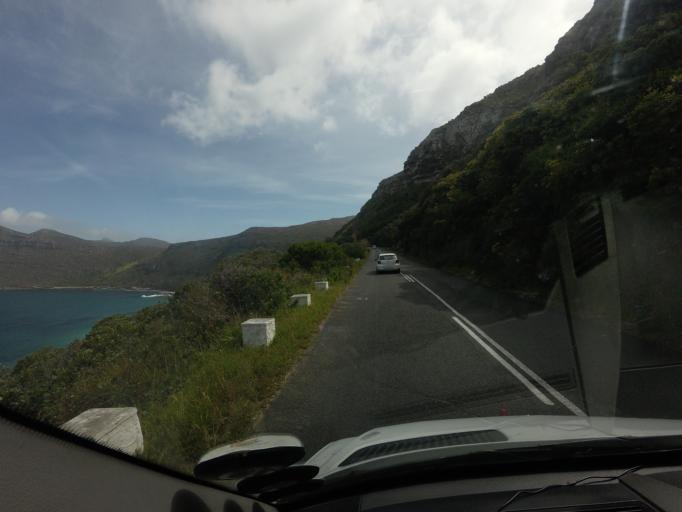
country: ZA
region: Western Cape
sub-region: City of Cape Town
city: Retreat
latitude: -34.2602
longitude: 18.4686
